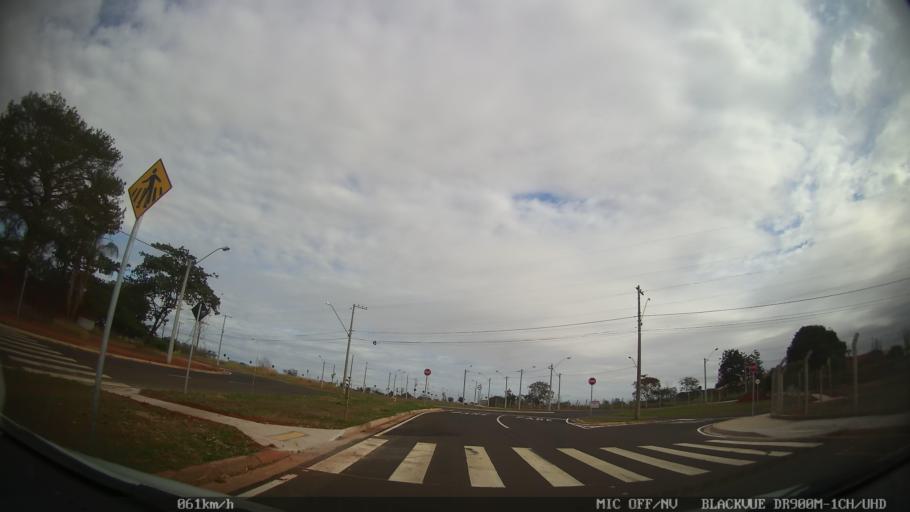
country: BR
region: Sao Paulo
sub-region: Sao Jose Do Rio Preto
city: Sao Jose do Rio Preto
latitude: -20.8274
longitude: -49.4145
